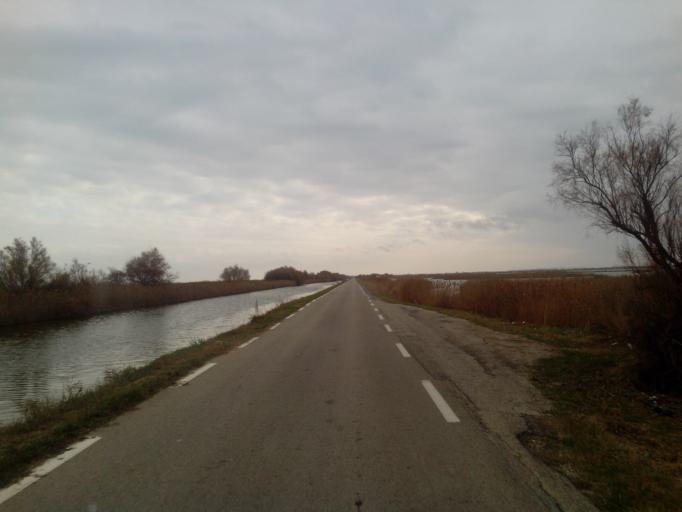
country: FR
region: Languedoc-Roussillon
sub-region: Departement du Gard
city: Vauvert
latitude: 43.6297
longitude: 4.3079
